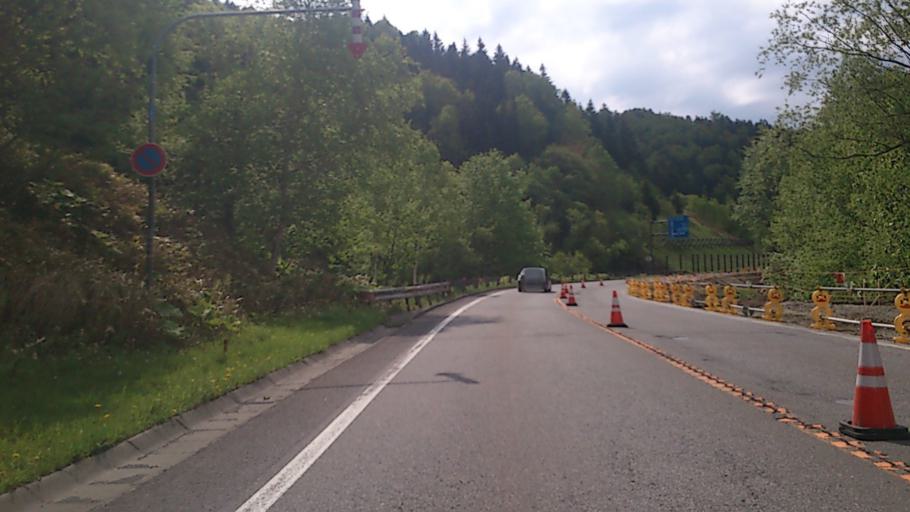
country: JP
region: Hokkaido
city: Kamikawa
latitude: 43.6831
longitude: 143.0341
